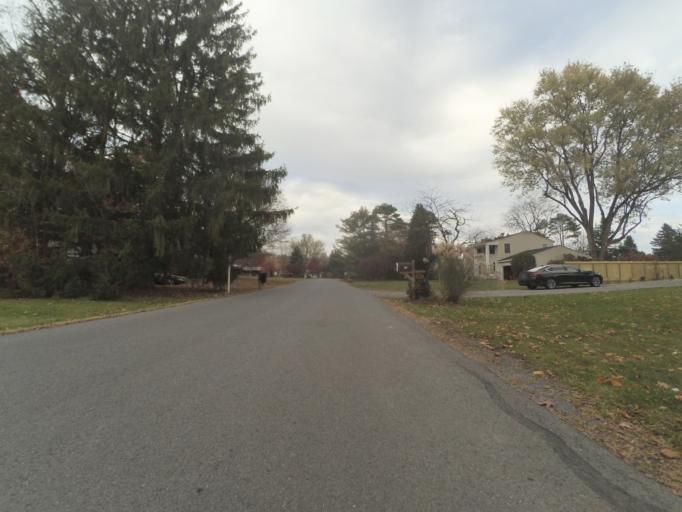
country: US
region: Pennsylvania
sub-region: Centre County
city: Boalsburg
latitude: 40.7805
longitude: -77.8172
